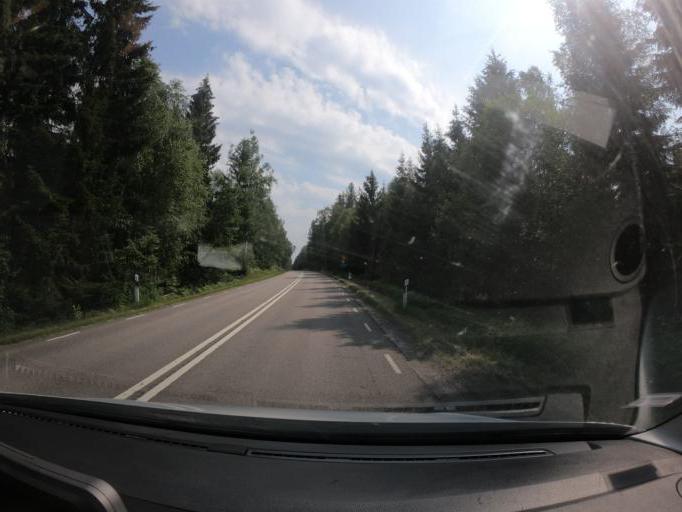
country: SE
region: Skane
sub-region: Hassleholms Kommun
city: Bjarnum
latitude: 56.3598
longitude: 13.6577
